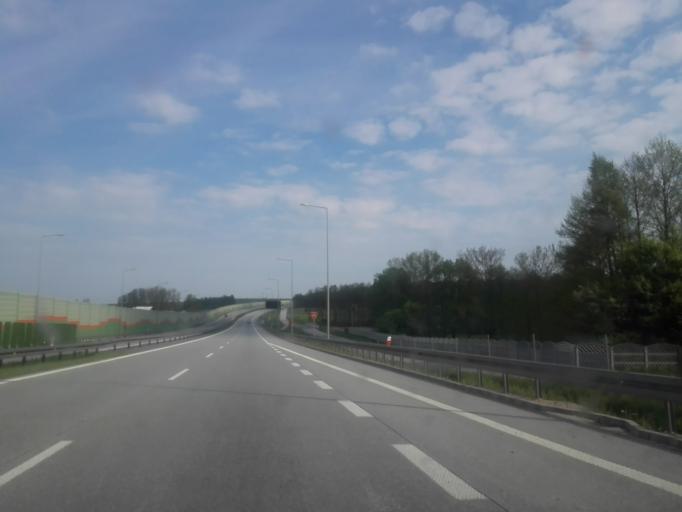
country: PL
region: Lodz Voivodeship
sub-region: Powiat rawski
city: Rawa Mazowiecka
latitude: 51.7070
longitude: 20.2201
